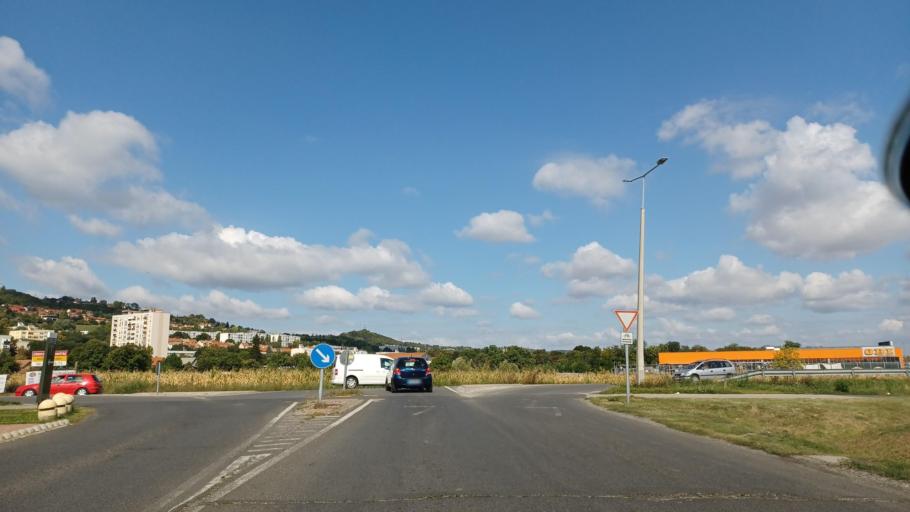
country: HU
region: Tolna
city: Szekszard
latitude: 46.3311
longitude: 18.7032
